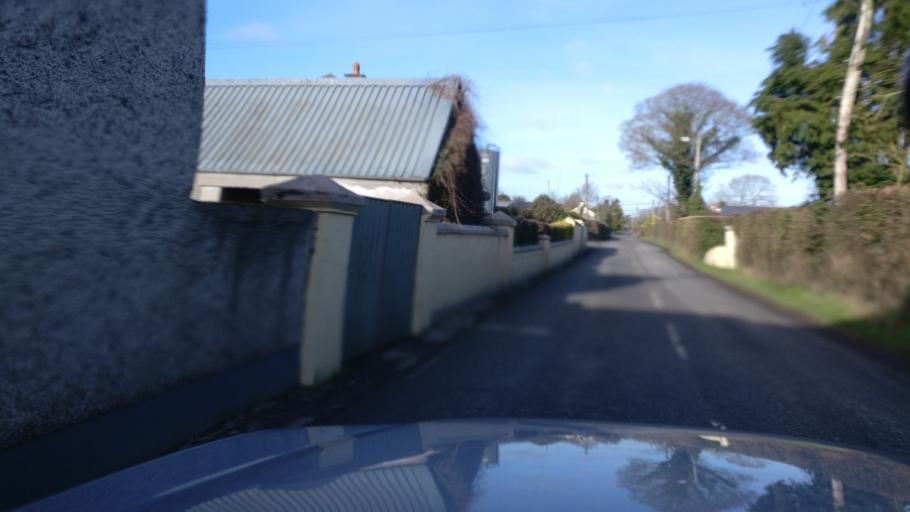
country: IE
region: Leinster
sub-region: Kilkenny
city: Castlecomer
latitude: 52.8640
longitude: -7.1647
